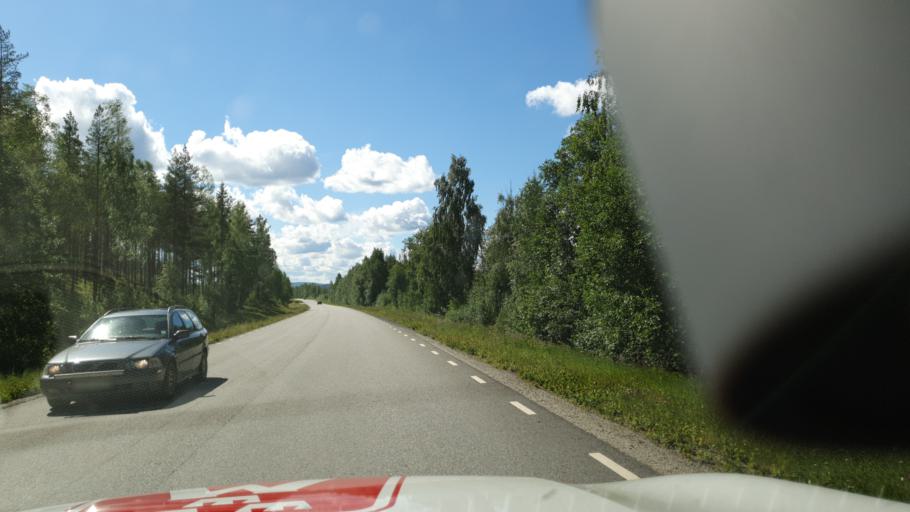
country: SE
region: Vaesterbotten
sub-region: Lycksele Kommun
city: Lycksele
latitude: 64.6557
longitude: 18.6612
